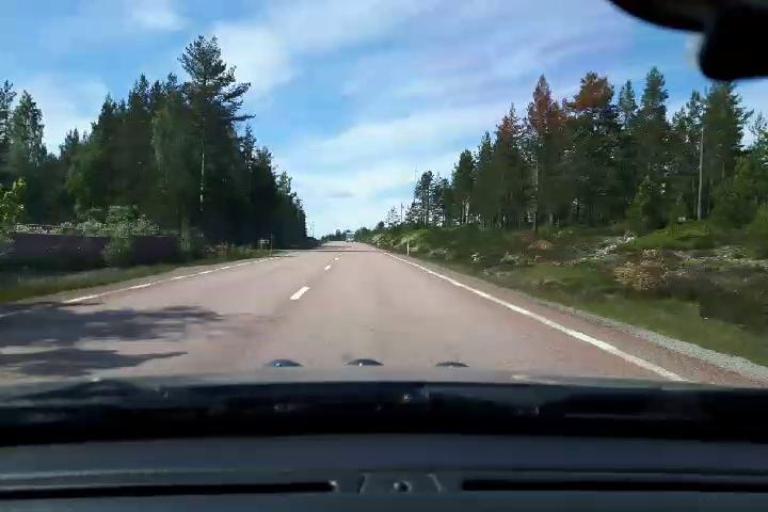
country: SE
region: Gaevleborg
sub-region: Soderhamns Kommun
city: Soderhamn
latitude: 61.1323
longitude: 16.9225
